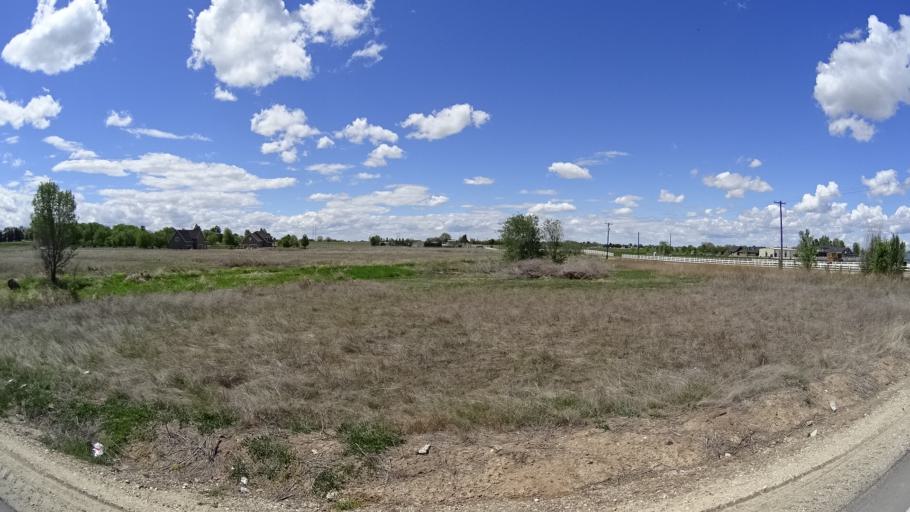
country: US
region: Idaho
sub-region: Ada County
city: Meridian
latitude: 43.5753
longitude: -116.4536
